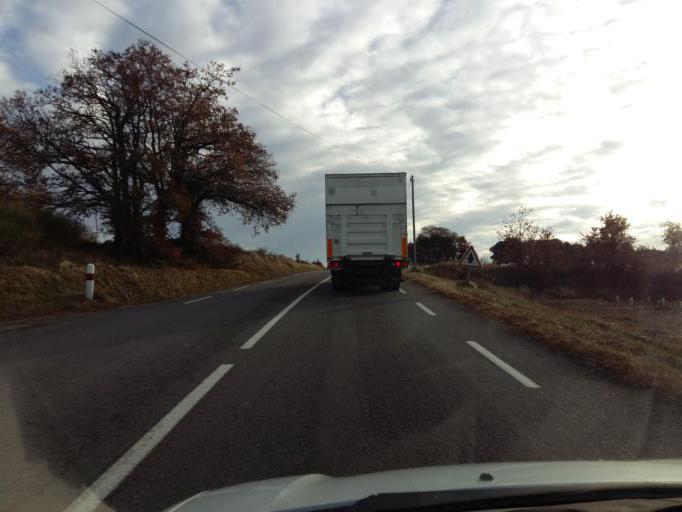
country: FR
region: Rhone-Alpes
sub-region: Departement de la Drome
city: Tulette
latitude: 44.2938
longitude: 4.9429
